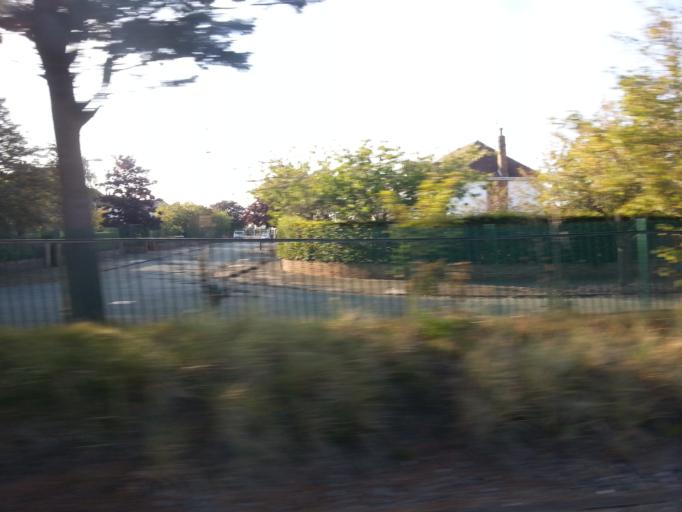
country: GB
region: England
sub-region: Sefton
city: Southport
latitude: 53.6264
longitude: -3.0211
